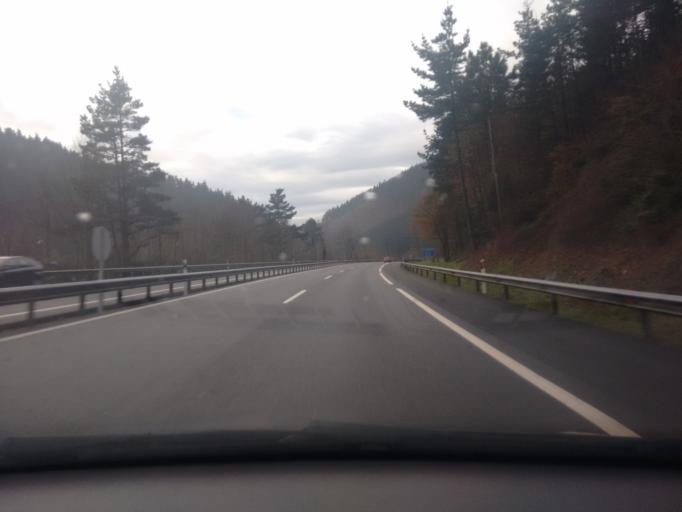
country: ES
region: Basque Country
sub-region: Provincia de Guipuzcoa
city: Mendaro
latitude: 43.2456
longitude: -2.3956
